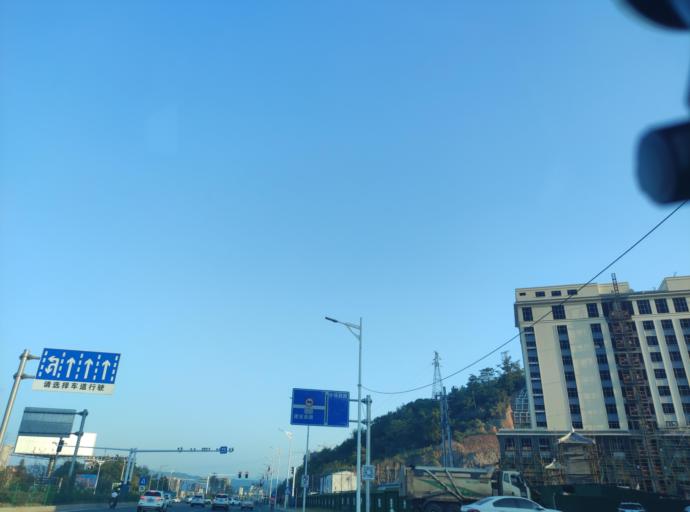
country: CN
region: Jiangxi Sheng
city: Pingxiang
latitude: 27.6441
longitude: 113.8253
